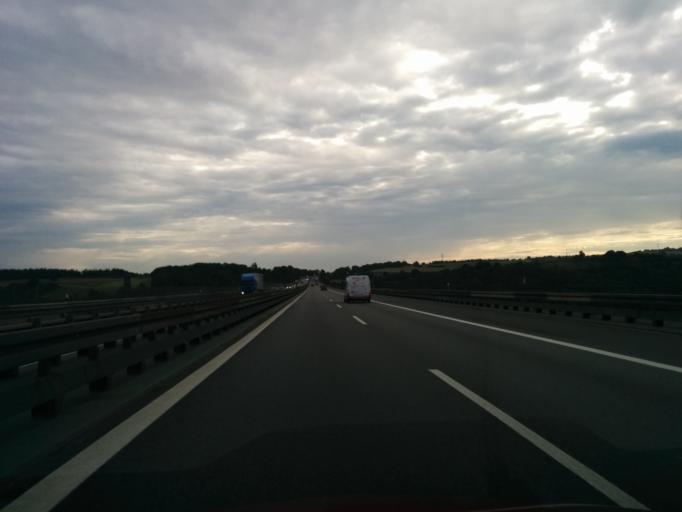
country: DE
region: Bavaria
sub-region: Upper Palatinate
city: Sinzing
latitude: 48.9962
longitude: 12.0328
